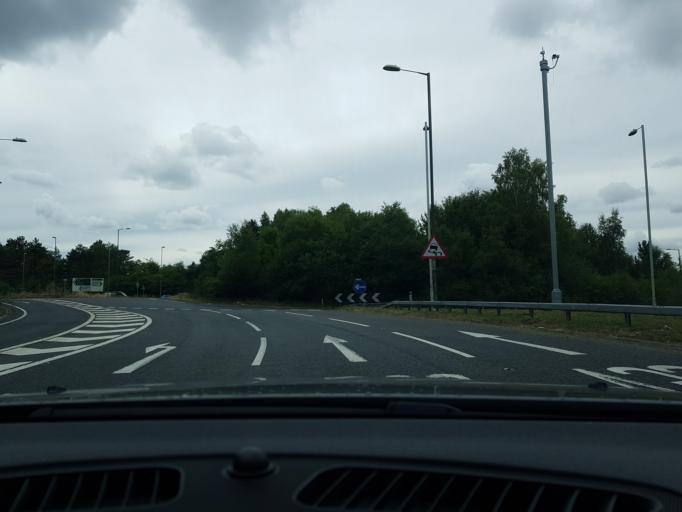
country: GB
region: England
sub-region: Hampshire
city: Basingstoke
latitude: 51.2759
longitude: -1.1109
